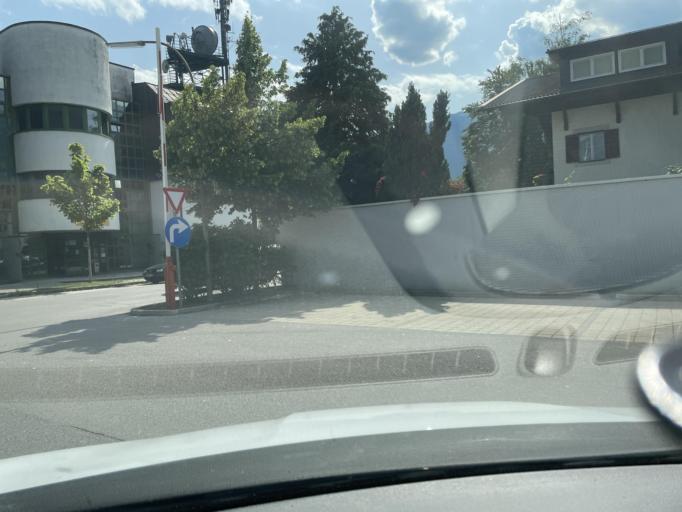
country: AT
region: Tyrol
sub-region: Politischer Bezirk Lienz
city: Lienz
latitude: 46.8321
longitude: 12.7776
